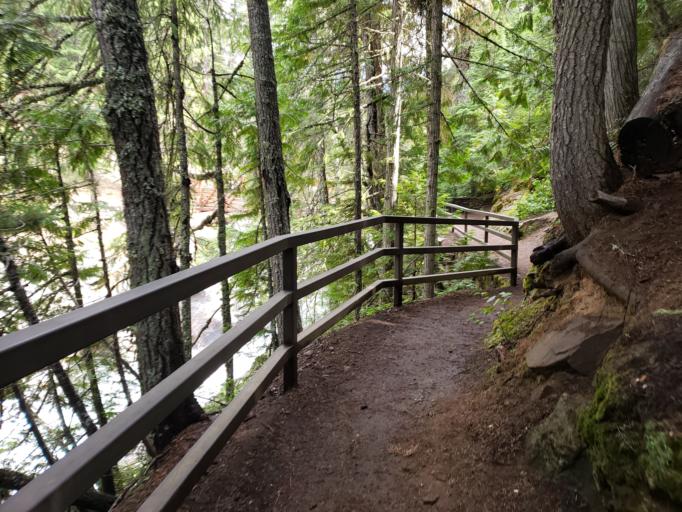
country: US
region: Washington
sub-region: Chelan County
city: Leavenworth
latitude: 47.6064
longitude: -120.8868
